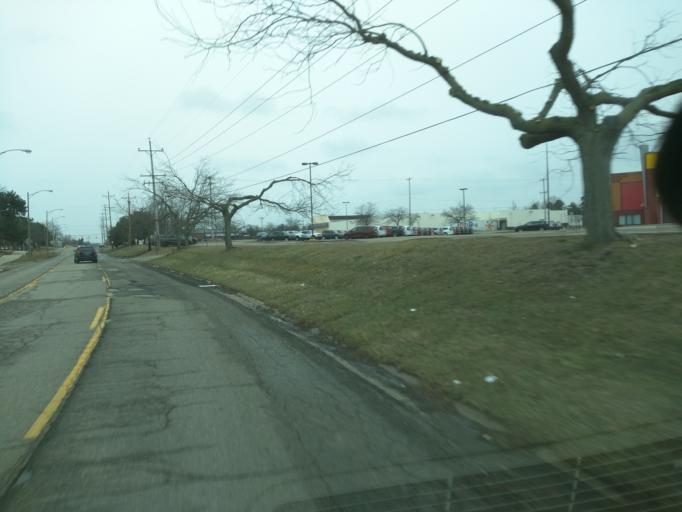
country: US
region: Michigan
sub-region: Eaton County
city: Waverly
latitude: 42.7442
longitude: -84.6323
